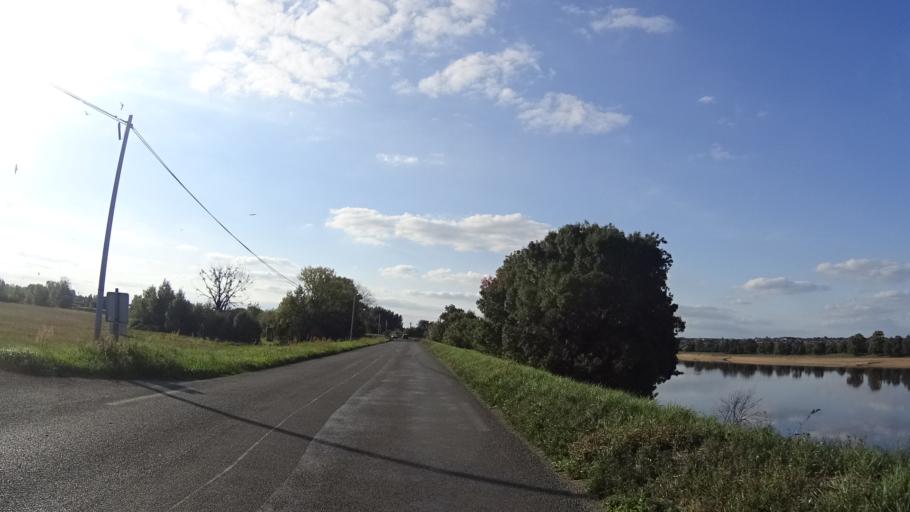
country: FR
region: Pays de la Loire
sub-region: Departement de Maine-et-Loire
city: Ingrandes
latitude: 47.3992
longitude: -0.9014
